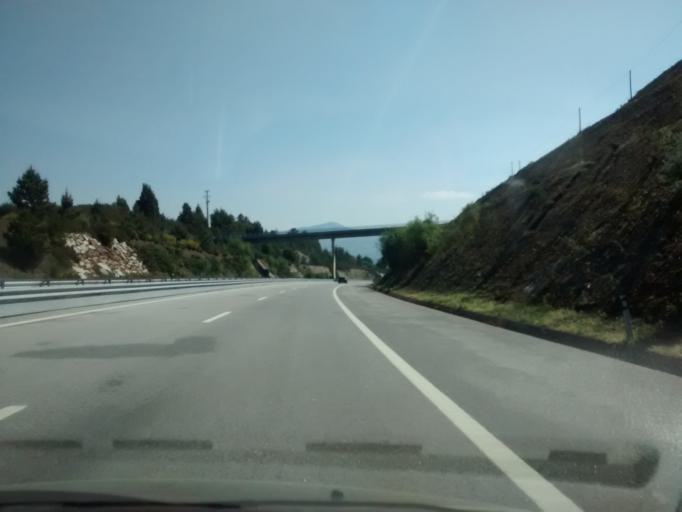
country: PT
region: Braga
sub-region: Cabeceiras de Basto
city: Cabeceiras de Basto
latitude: 41.4758
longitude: -7.9621
